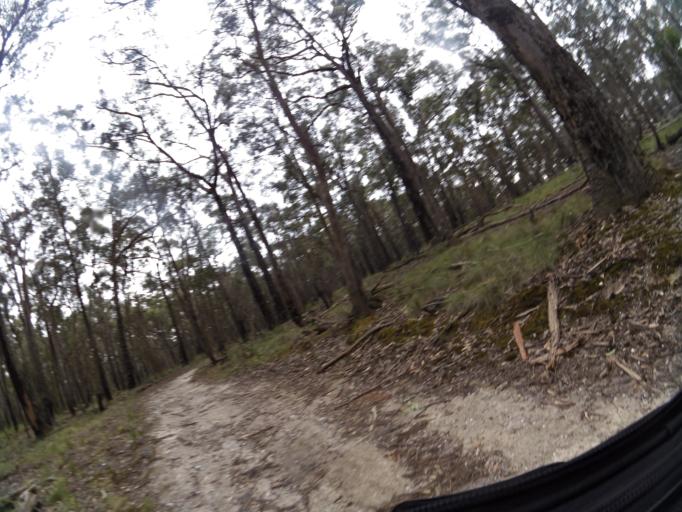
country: AU
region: Victoria
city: Brown Hill
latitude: -37.5348
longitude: 143.9011
